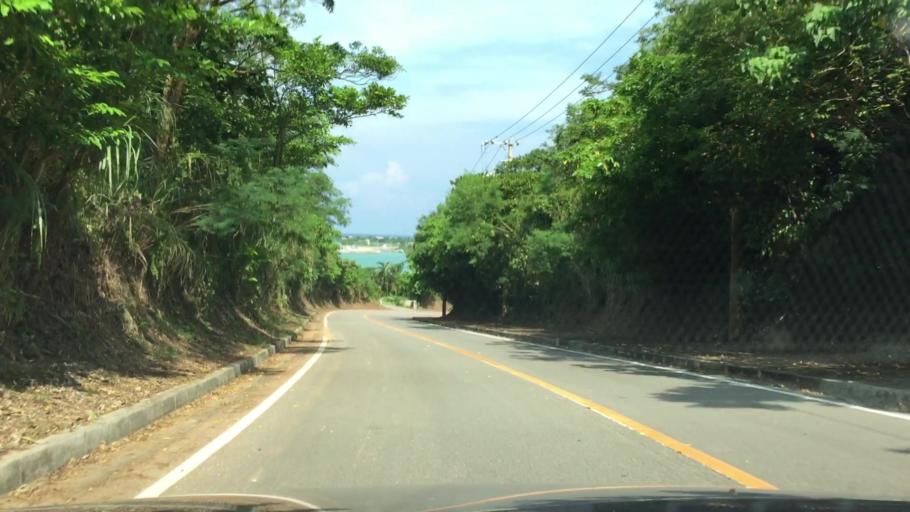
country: JP
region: Okinawa
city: Ishigaki
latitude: 24.5097
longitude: 124.2685
